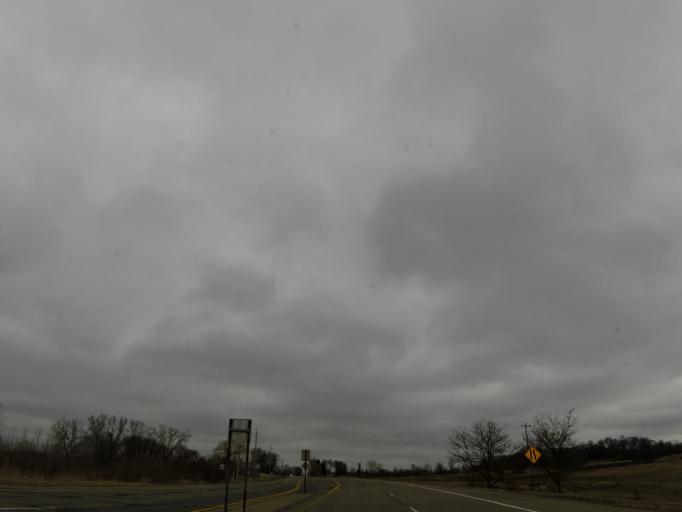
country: US
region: Minnesota
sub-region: Scott County
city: Shakopee
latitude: 44.7744
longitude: -93.5411
